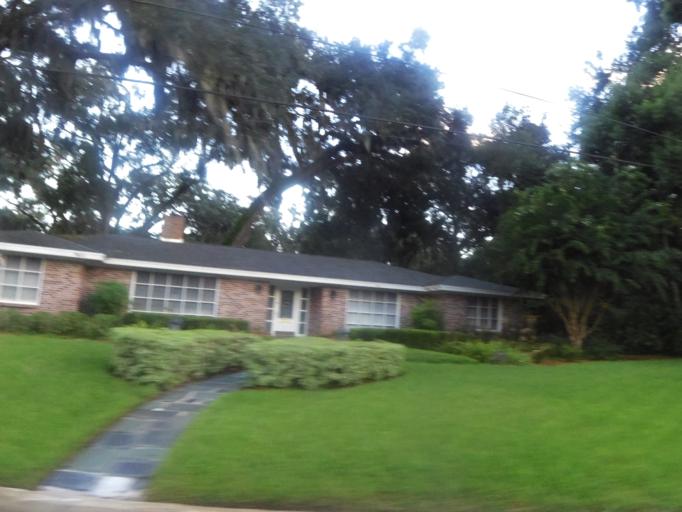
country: US
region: Florida
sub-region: Duval County
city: Jacksonville
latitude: 30.2357
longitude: -81.6232
